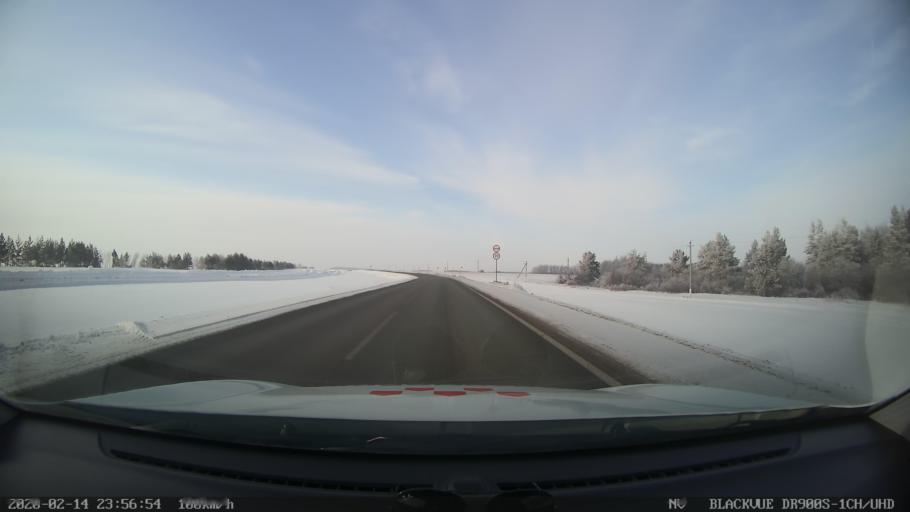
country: RU
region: Tatarstan
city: Kuybyshevskiy Zaton
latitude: 55.3296
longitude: 49.1218
